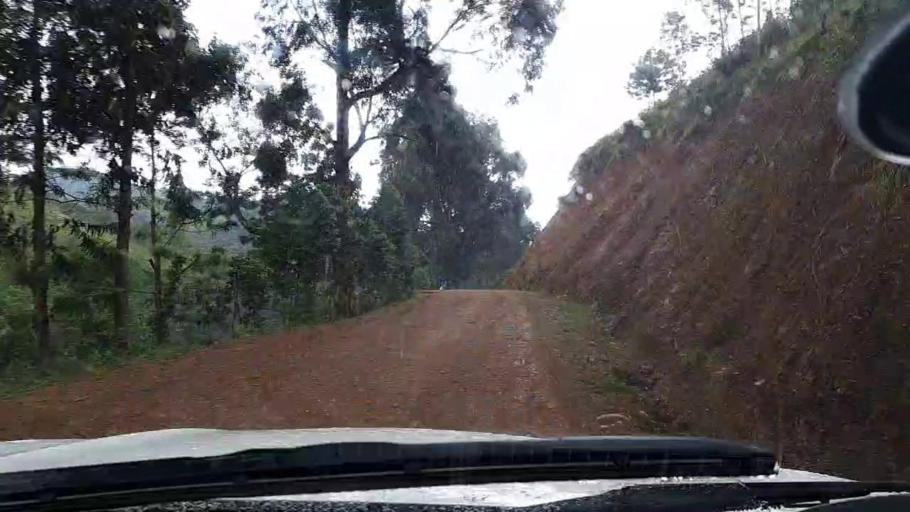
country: RW
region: Western Province
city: Kibuye
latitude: -2.1573
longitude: 29.4326
